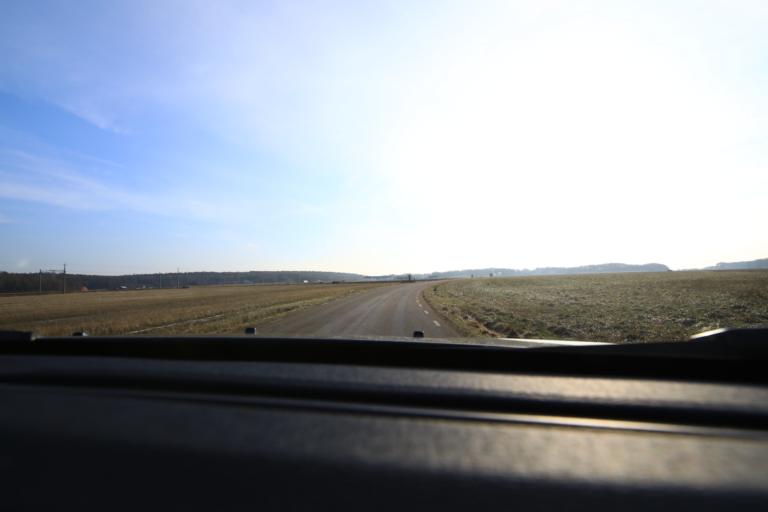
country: SE
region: Halland
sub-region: Varbergs Kommun
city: Varberg
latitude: 57.2046
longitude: 12.2195
